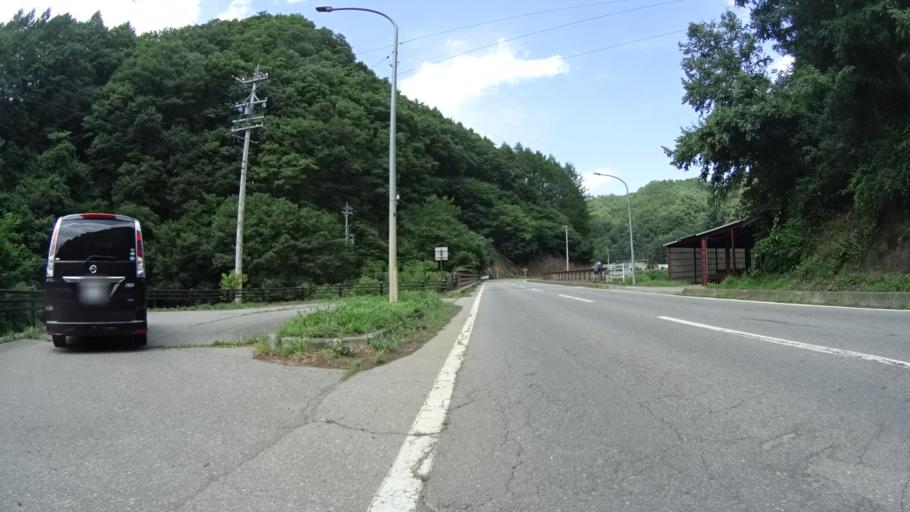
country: JP
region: Nagano
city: Saku
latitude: 36.0628
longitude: 138.5029
